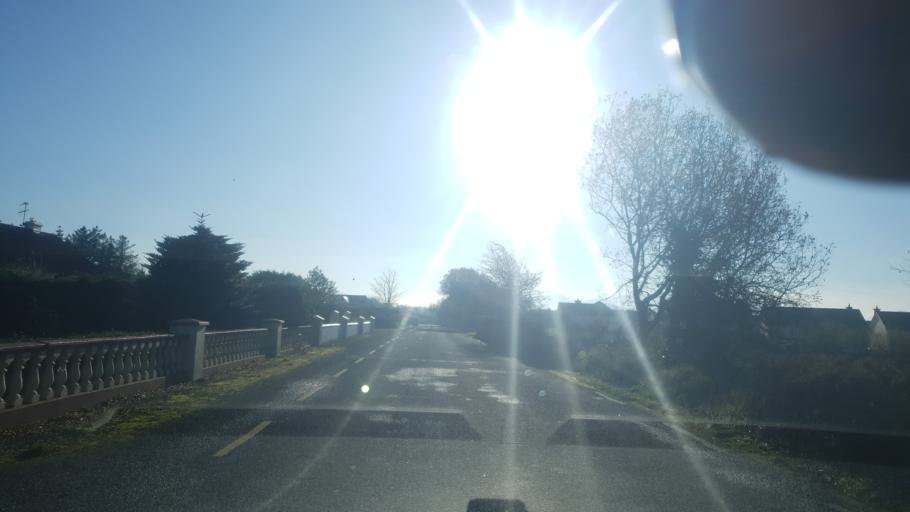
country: IE
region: Munster
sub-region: Ciarrai
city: Cill Airne
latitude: 52.1020
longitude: -9.4723
